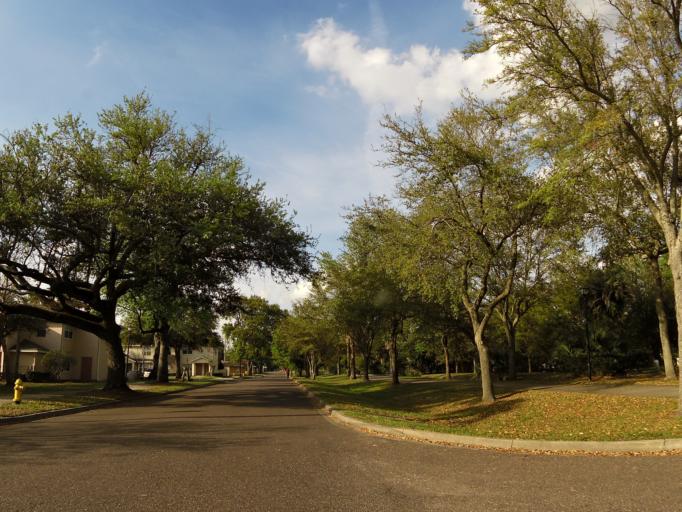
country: US
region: Florida
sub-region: Duval County
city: Jacksonville
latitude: 30.3452
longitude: -81.6715
